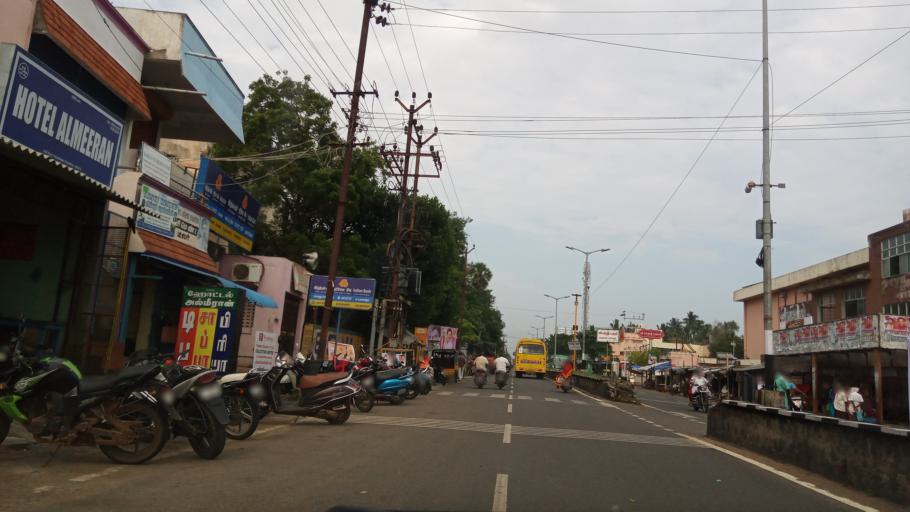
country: IN
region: Tamil Nadu
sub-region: Villupuram
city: Auroville
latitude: 12.0294
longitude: 79.8633
